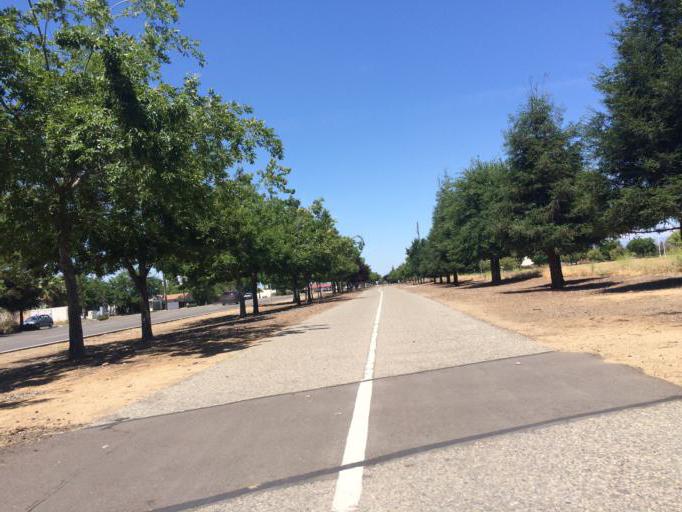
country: US
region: California
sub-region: Fresno County
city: Tarpey Village
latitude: 36.8024
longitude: -119.7000
